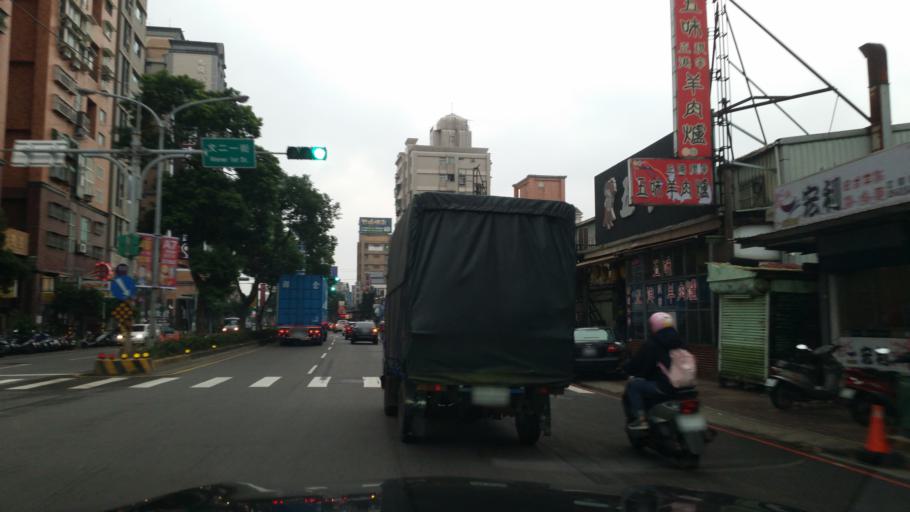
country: TW
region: Taiwan
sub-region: Taoyuan
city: Taoyuan
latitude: 25.0603
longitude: 121.3620
